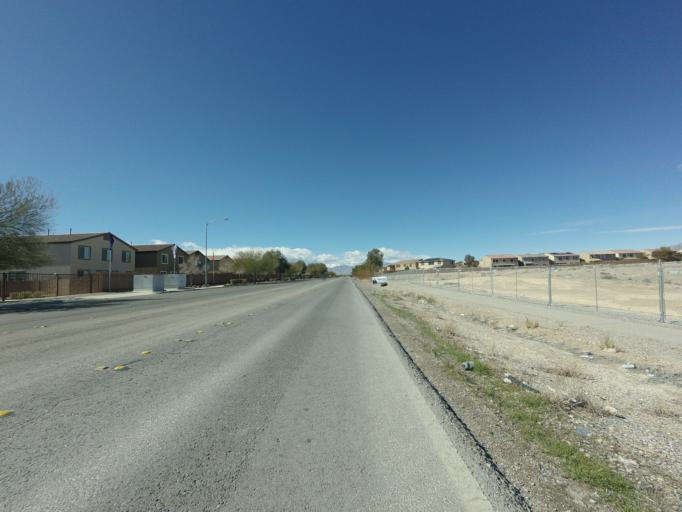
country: US
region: Nevada
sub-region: Clark County
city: Nellis Air Force Base
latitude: 36.2693
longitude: -115.0833
